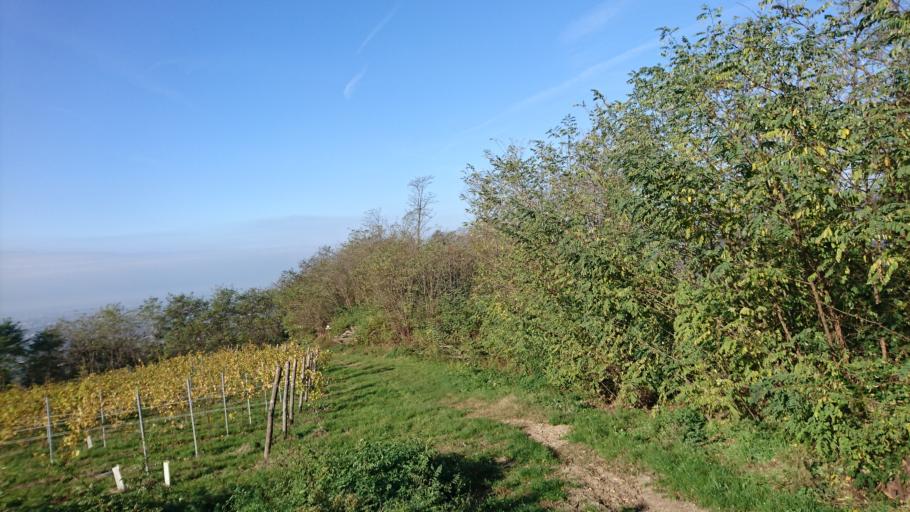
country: IT
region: Veneto
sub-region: Provincia di Padova
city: Fontanafredda
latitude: 45.3249
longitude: 11.6848
